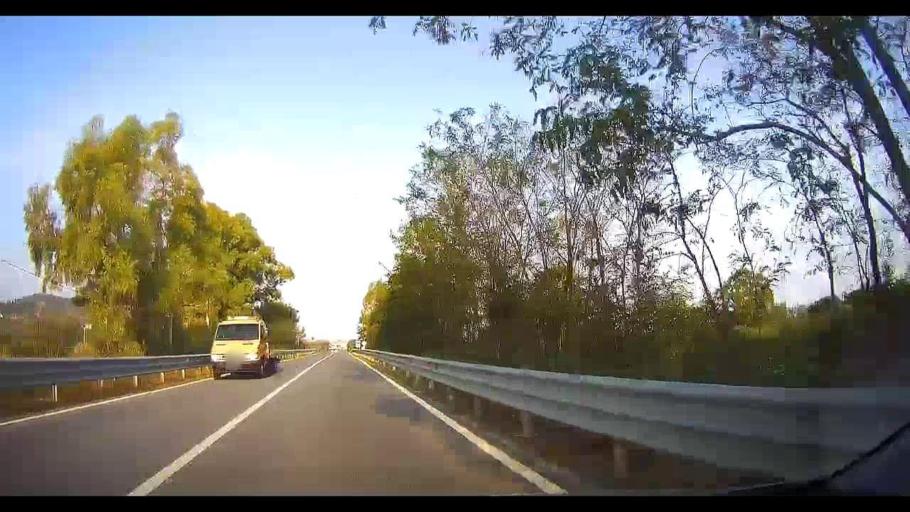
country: IT
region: Calabria
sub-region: Provincia di Cosenza
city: Cariati
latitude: 39.5215
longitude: 16.9012
